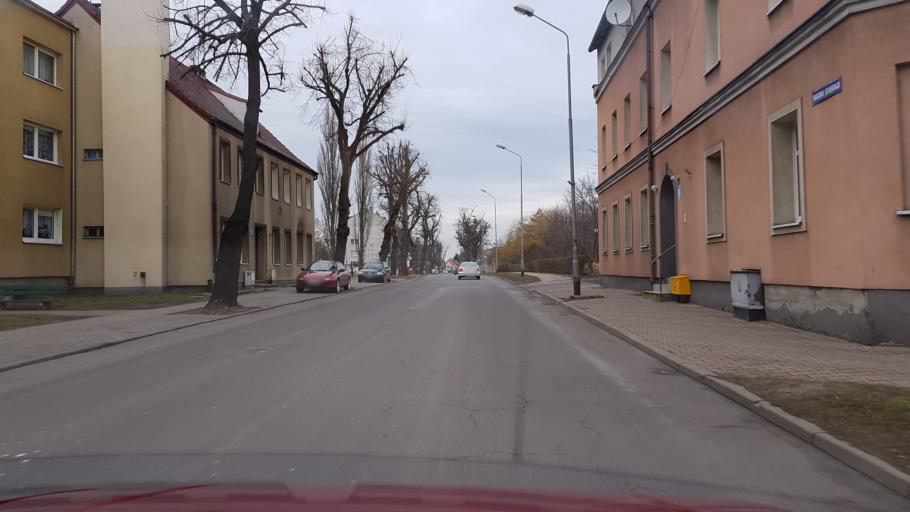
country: PL
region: West Pomeranian Voivodeship
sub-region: Powiat policki
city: Police
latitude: 53.5491
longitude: 14.5724
